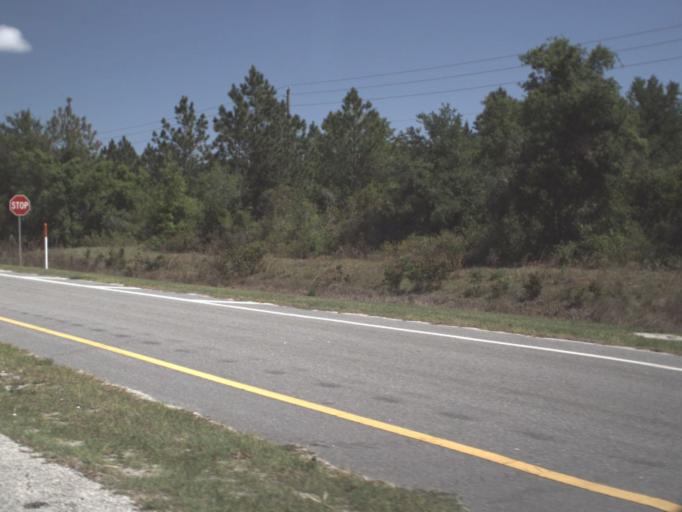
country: US
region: Florida
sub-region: Flagler County
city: Palm Coast
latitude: 29.5589
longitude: -81.2679
